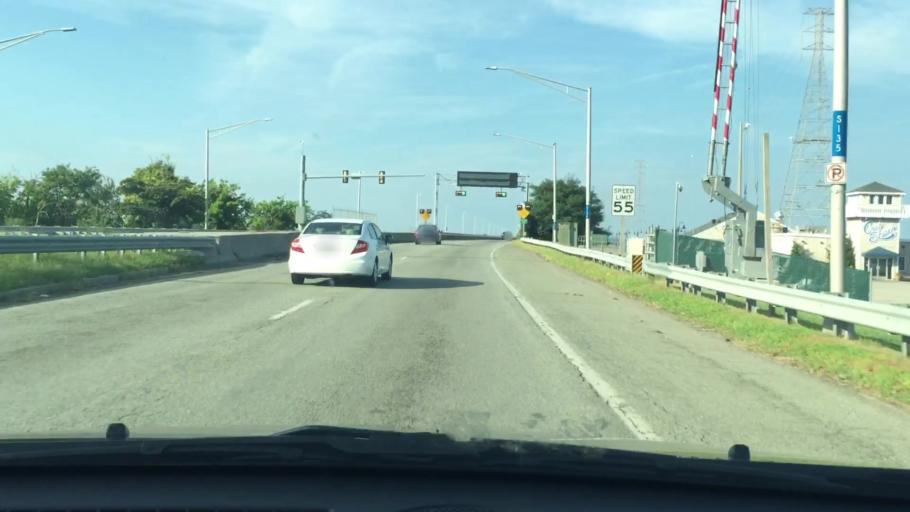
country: US
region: Virginia
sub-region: City of Newport News
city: Newport News
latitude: 37.0138
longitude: -76.4555
